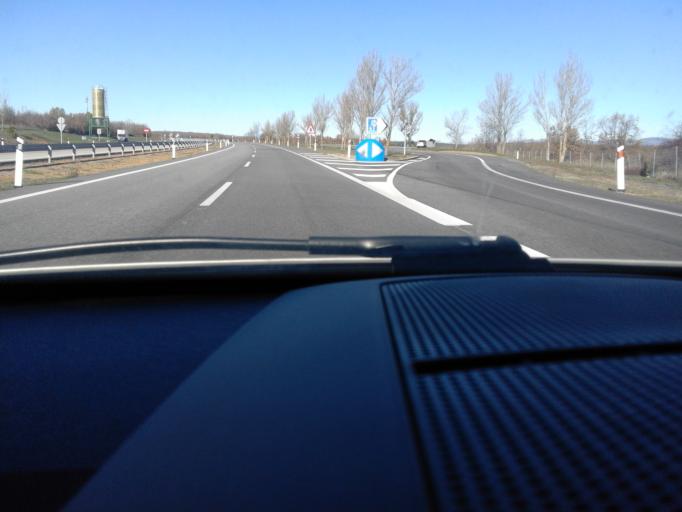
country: ES
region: Castille and Leon
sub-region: Provincia de Leon
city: Valverde de la Virgen
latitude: 42.6129
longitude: -5.7309
